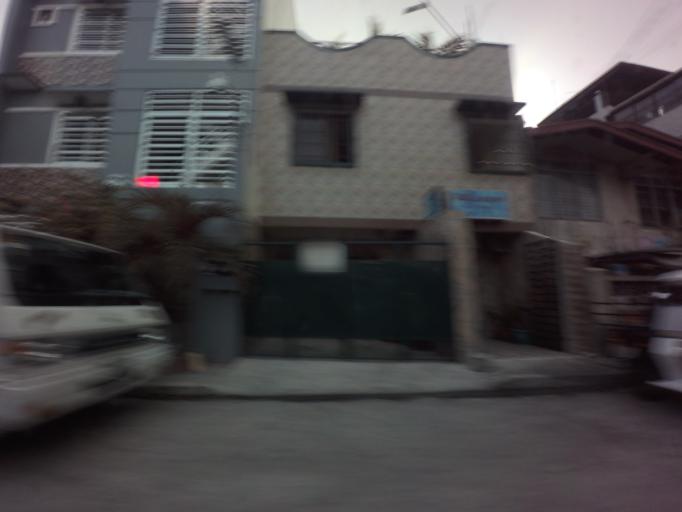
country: PH
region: Metro Manila
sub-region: Makati City
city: Makati City
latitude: 14.5634
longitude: 121.0491
